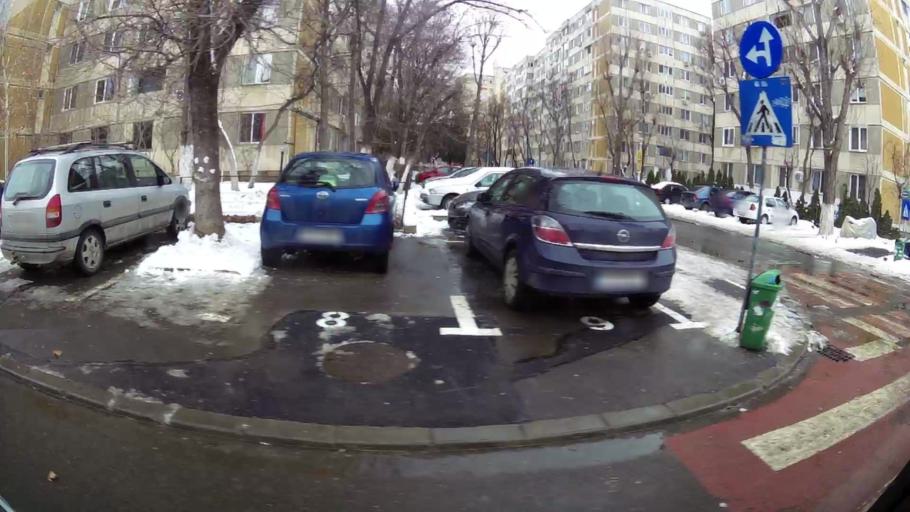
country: RO
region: Ilfov
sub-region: Comuna Popesti-Leordeni
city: Popesti-Leordeni
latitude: 44.3883
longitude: 26.1300
